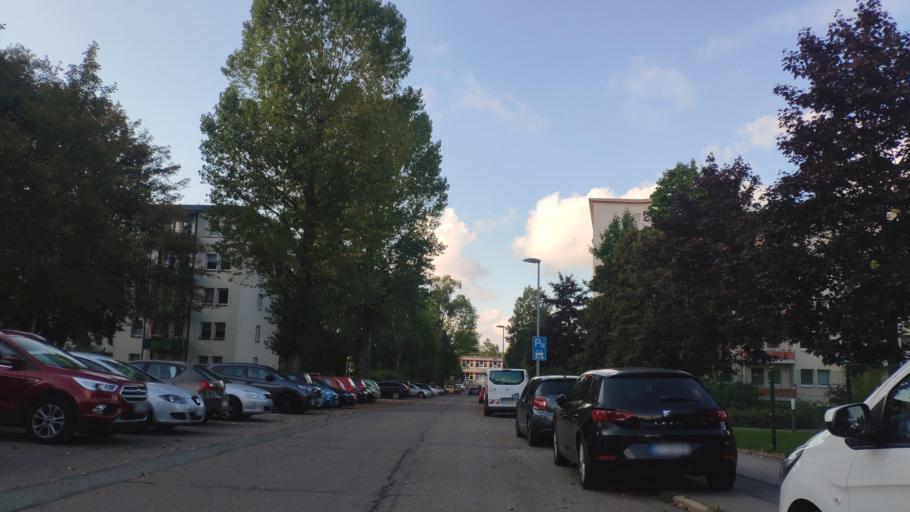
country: DE
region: Saxony
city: Chemnitz
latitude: 50.8204
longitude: 12.9589
